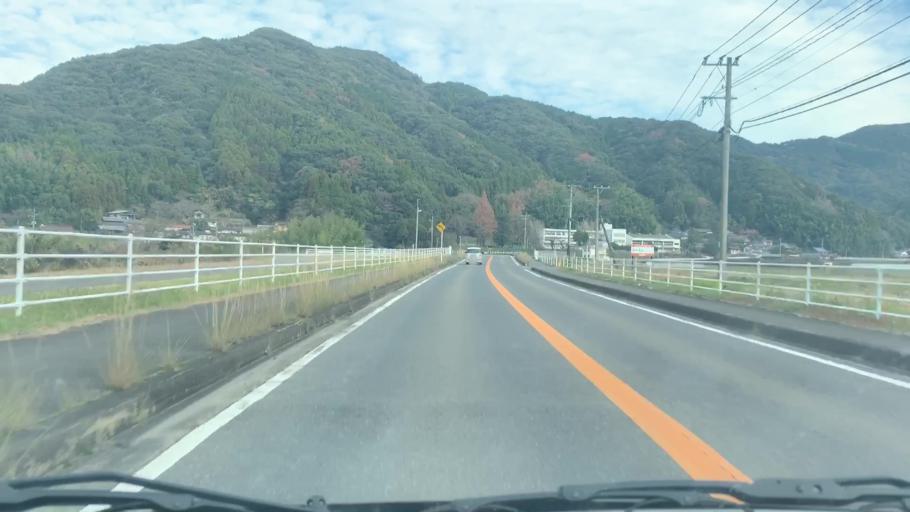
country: JP
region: Saga Prefecture
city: Karatsu
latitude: 33.3609
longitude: 130.0090
